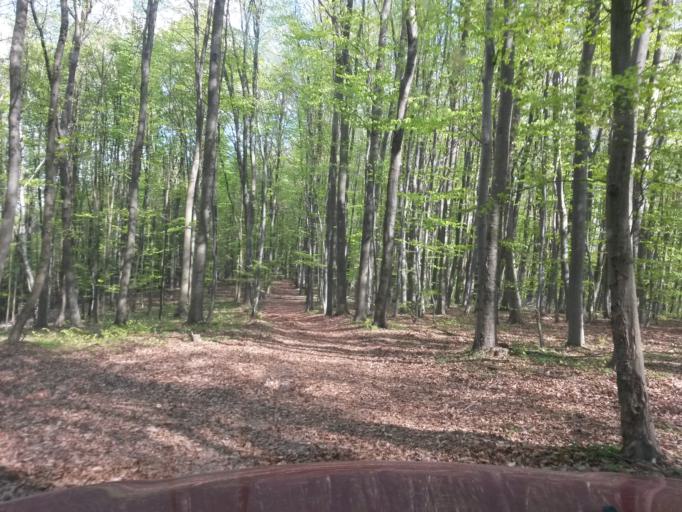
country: SK
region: Presovsky
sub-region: Okres Presov
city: Presov
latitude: 48.9491
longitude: 21.1525
